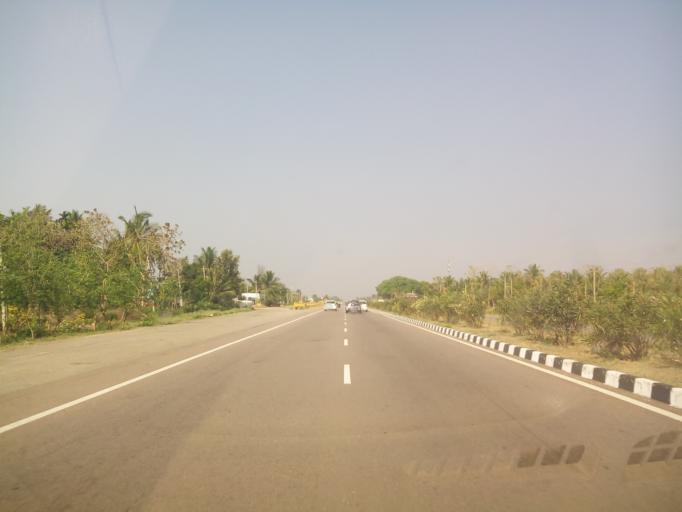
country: IN
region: Karnataka
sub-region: Tumkur
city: Kunigal
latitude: 12.9948
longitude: 76.8999
